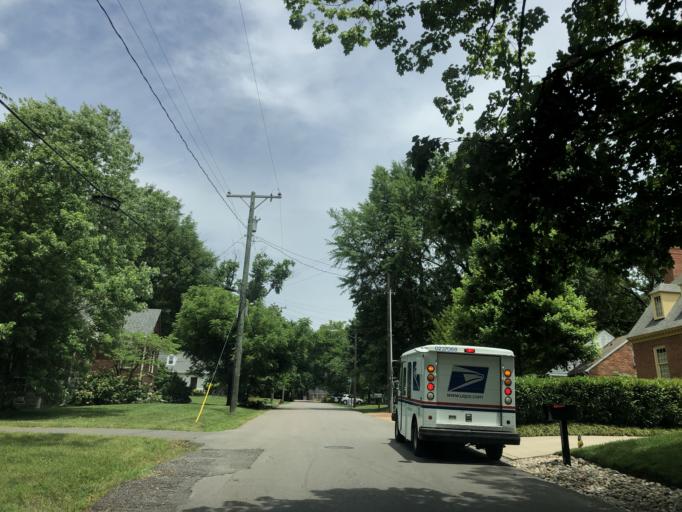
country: US
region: Tennessee
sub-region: Davidson County
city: Oak Hill
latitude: 36.1020
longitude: -86.8040
